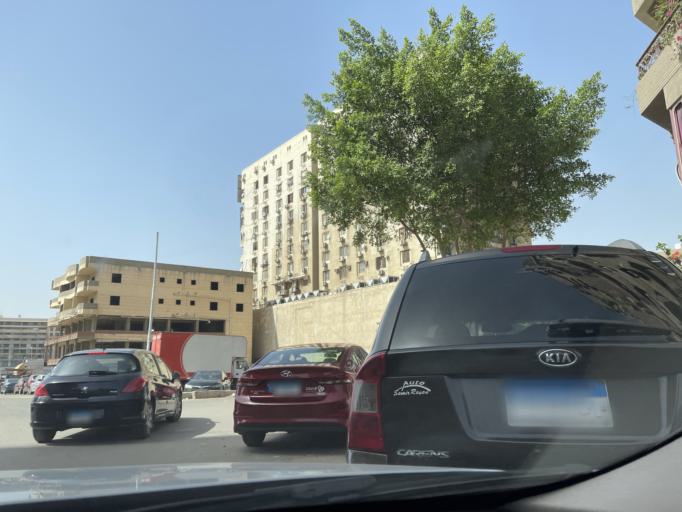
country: EG
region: Muhafazat al Qahirah
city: Cairo
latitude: 30.0686
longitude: 31.3552
